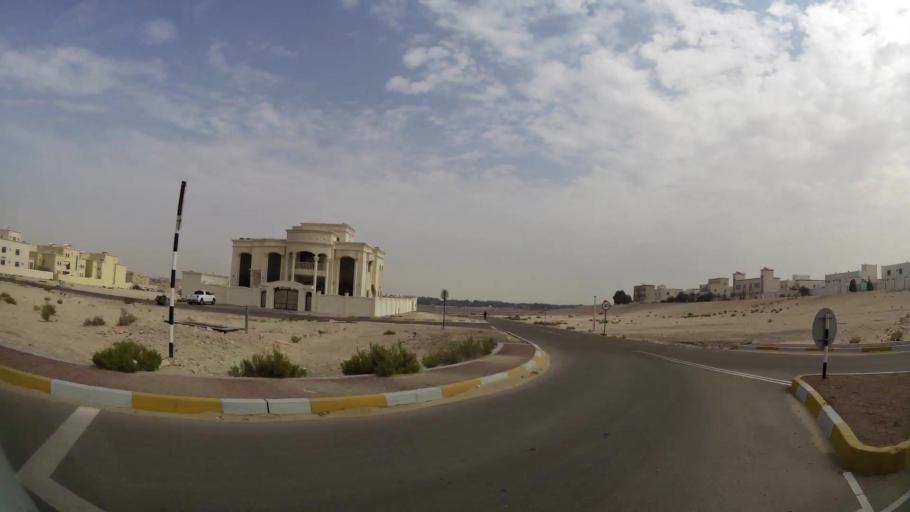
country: AE
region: Abu Dhabi
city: Abu Dhabi
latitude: 24.2988
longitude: 54.6584
